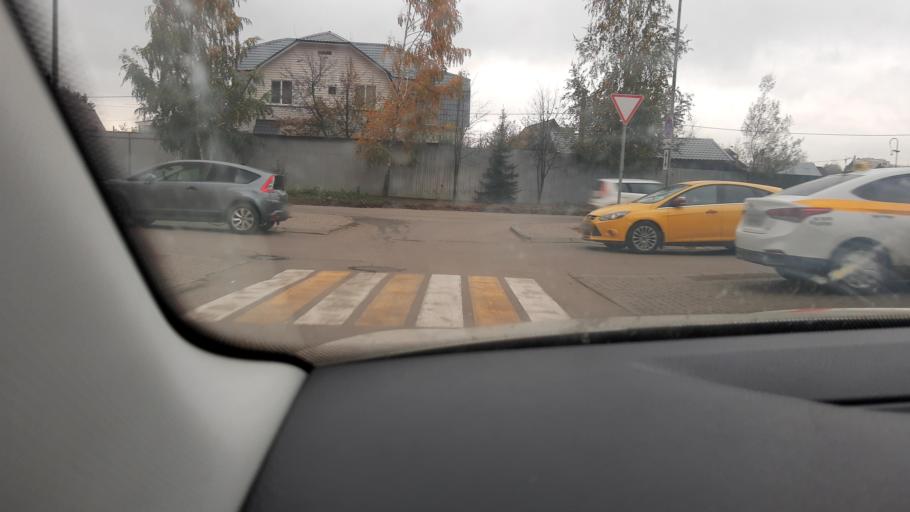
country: RU
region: Moskovskaya
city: Shcherbinka
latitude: 55.5032
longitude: 37.5365
